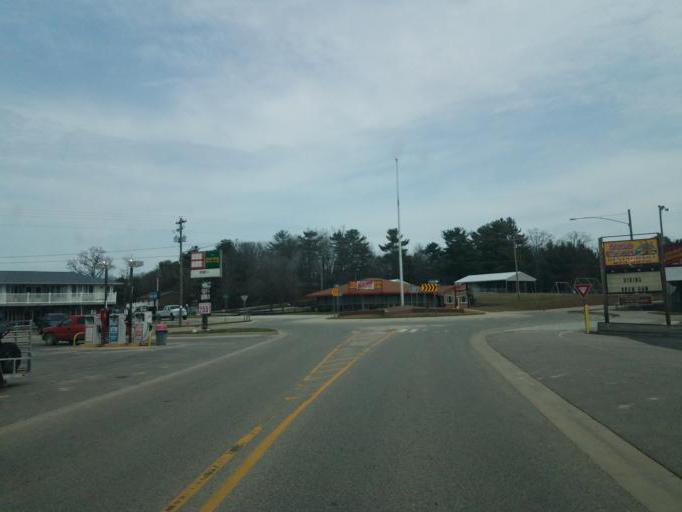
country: US
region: Michigan
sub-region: Oceana County
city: Hart
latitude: 43.6672
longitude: -86.4886
